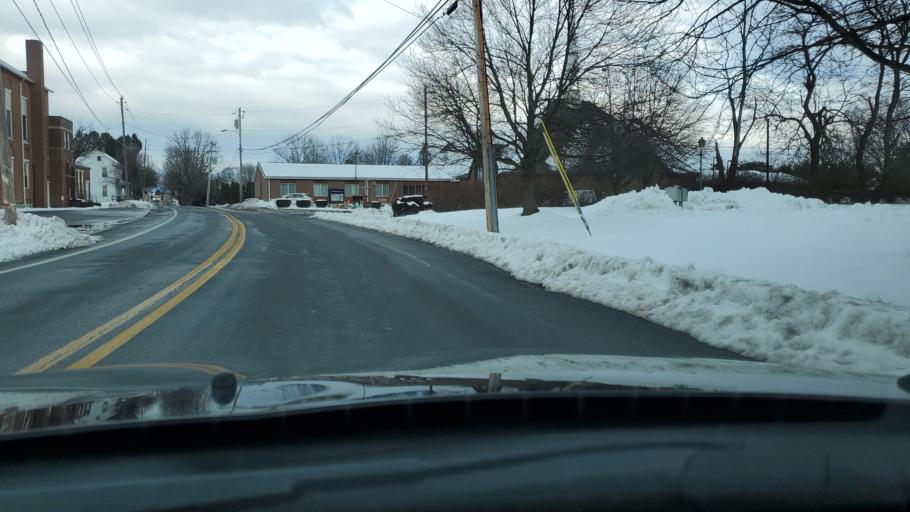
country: US
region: Pennsylvania
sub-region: Cumberland County
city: Mechanicsburg
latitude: 40.2082
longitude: -77.0305
